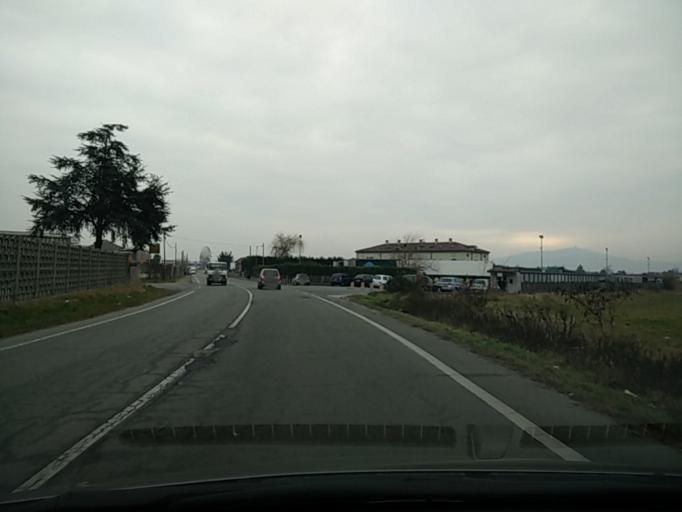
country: IT
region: Piedmont
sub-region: Provincia di Torino
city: Leini
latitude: 45.1584
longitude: 7.7151
